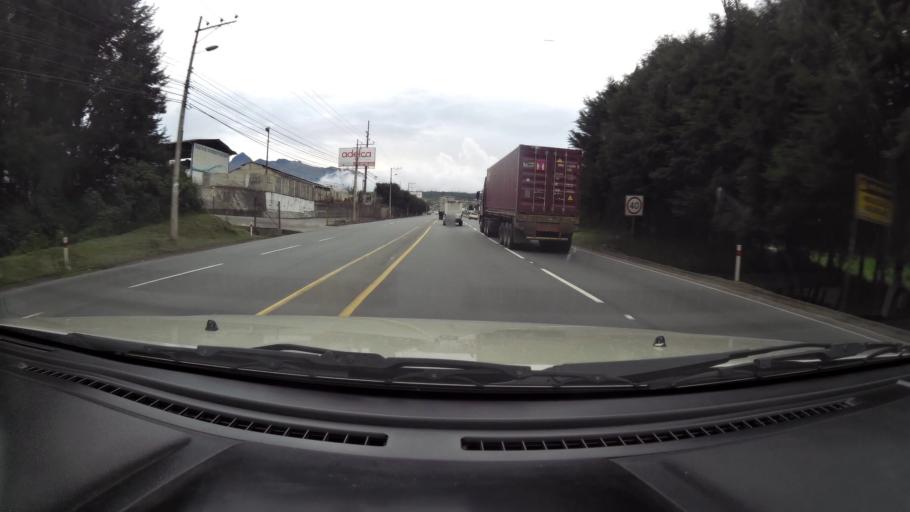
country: EC
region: Pichincha
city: Machachi
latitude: -0.4425
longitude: -78.6276
